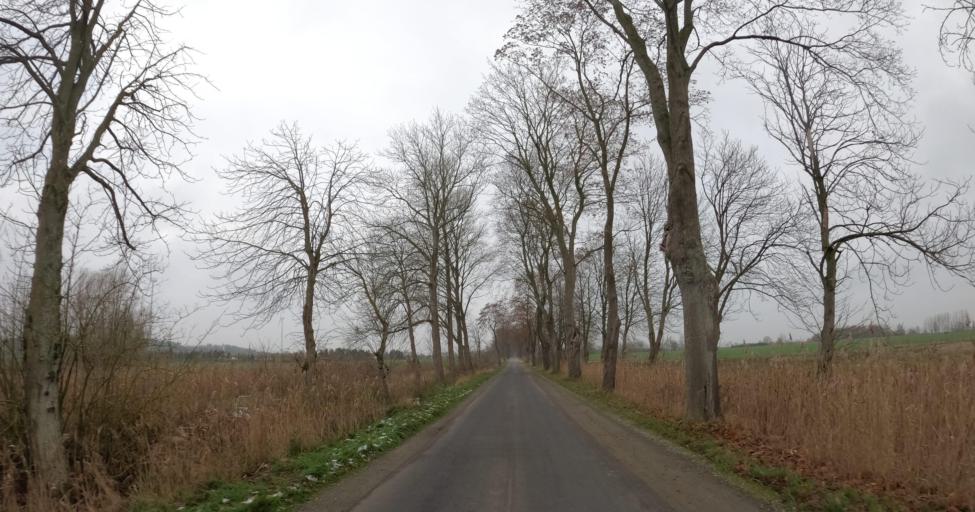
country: PL
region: West Pomeranian Voivodeship
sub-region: Powiat bialogardzki
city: Karlino
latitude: 53.9777
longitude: 15.8721
